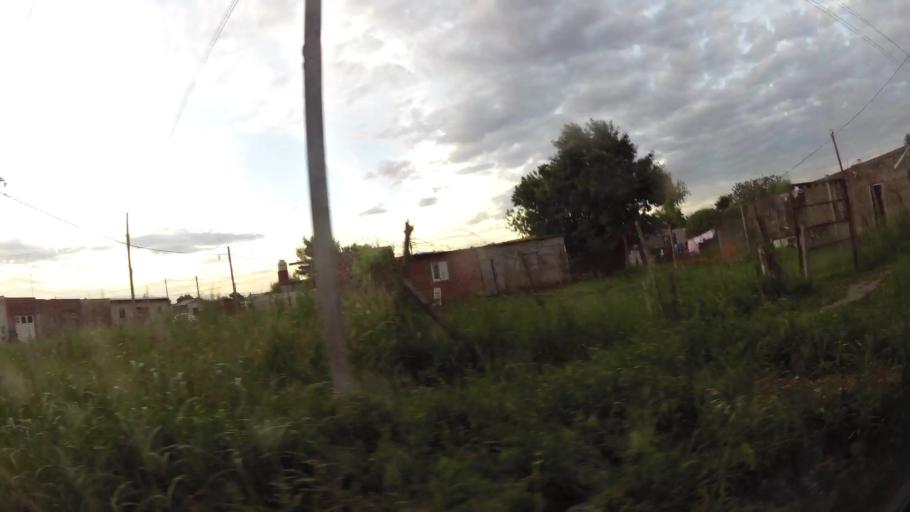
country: AR
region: Buenos Aires
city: San Nicolas de los Arroyos
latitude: -33.3181
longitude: -60.2455
